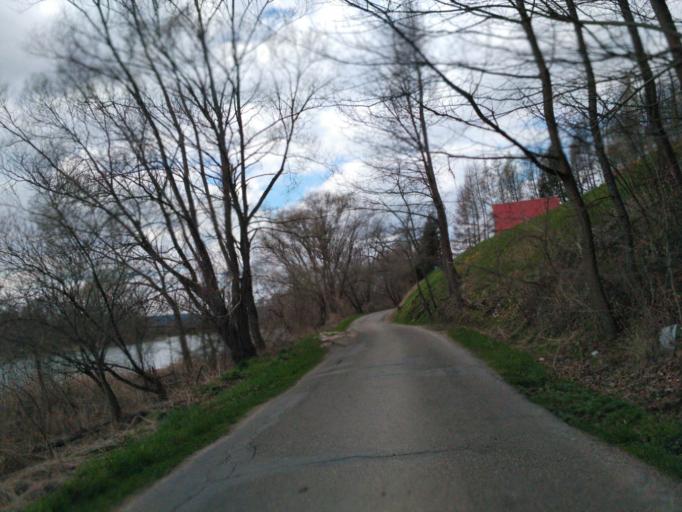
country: PL
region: Subcarpathian Voivodeship
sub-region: Powiat sanocki
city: Tyrawa Woloska
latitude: 49.6631
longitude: 22.2951
